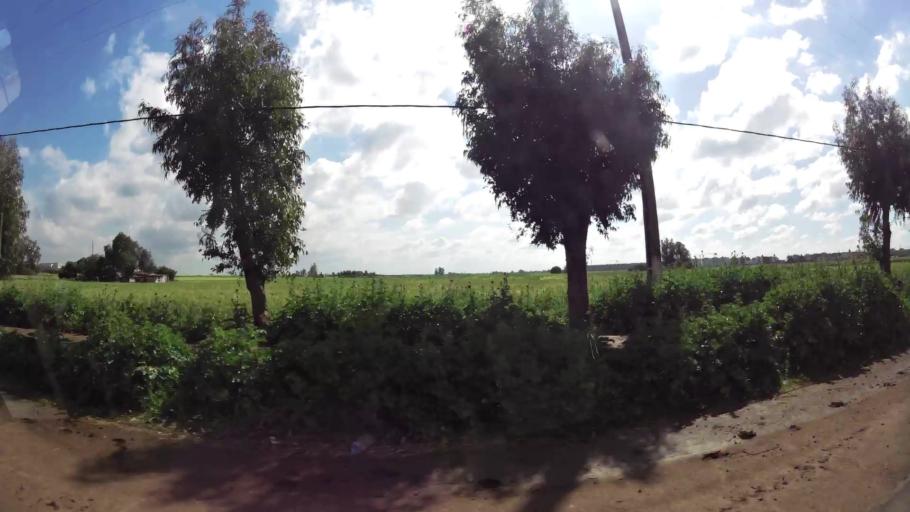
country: MA
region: Grand Casablanca
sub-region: Mediouna
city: Mediouna
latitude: 33.4475
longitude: -7.5042
